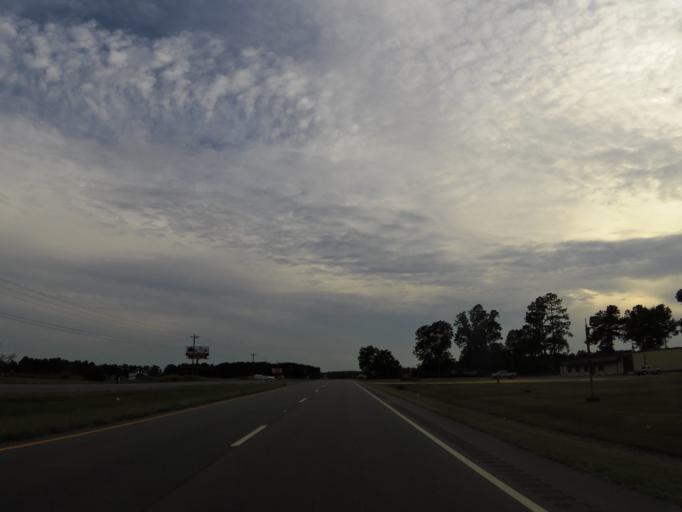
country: US
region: Alabama
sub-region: Escambia County
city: Atmore
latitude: 31.0700
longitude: -87.4873
